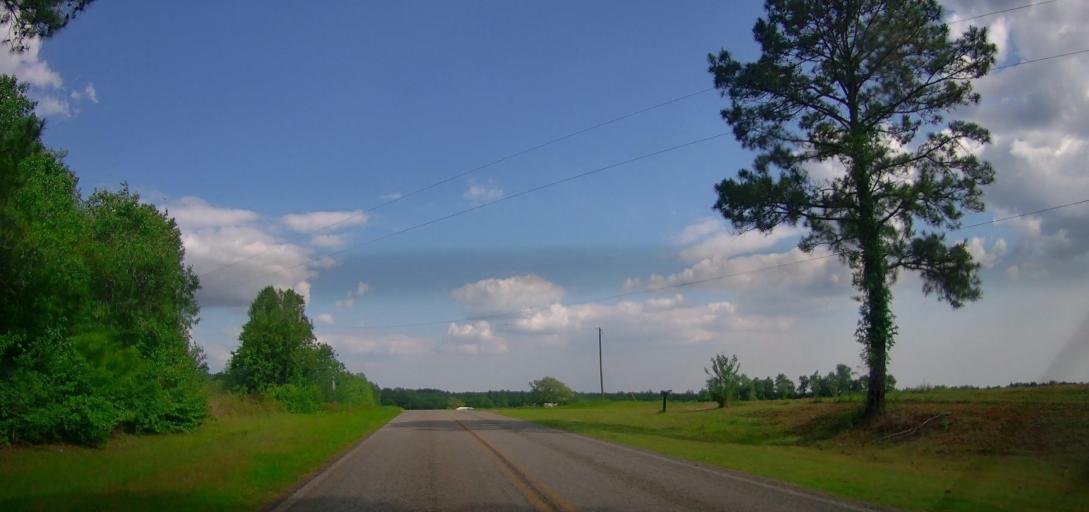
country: US
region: Georgia
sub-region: Laurens County
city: East Dublin
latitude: 32.6971
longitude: -82.9102
